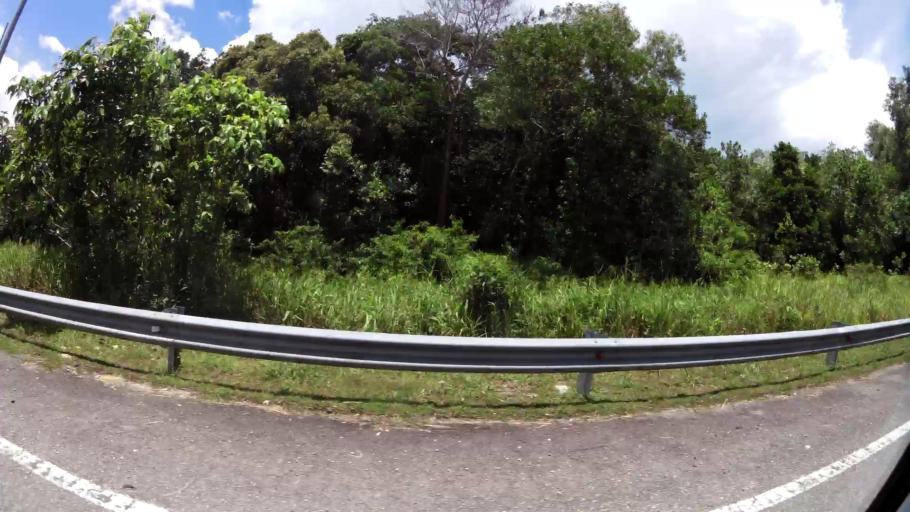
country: BN
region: Brunei and Muara
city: Bandar Seri Begawan
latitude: 4.9522
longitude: 114.8979
